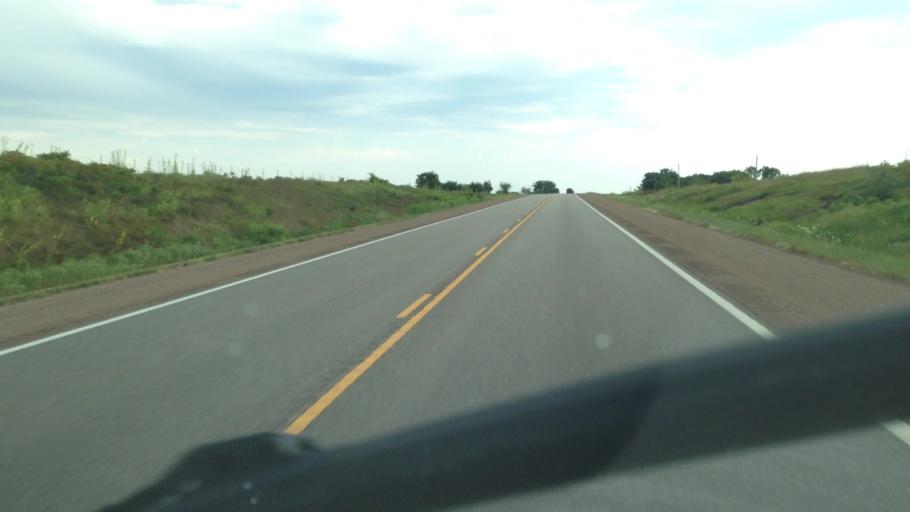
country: US
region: Kansas
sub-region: Woodson County
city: Yates Center
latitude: 38.0093
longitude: -95.7390
